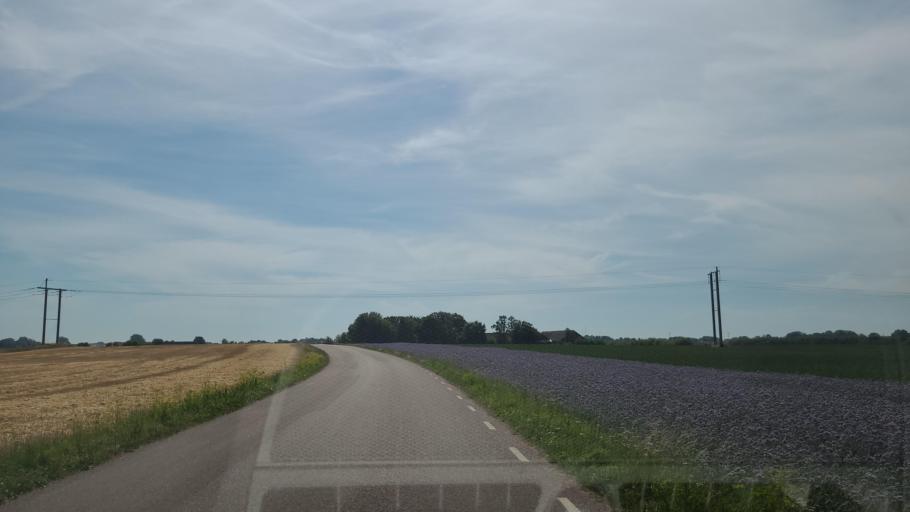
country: SE
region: Skane
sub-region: Trelleborgs Kommun
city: Skare
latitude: 55.4172
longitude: 13.0834
